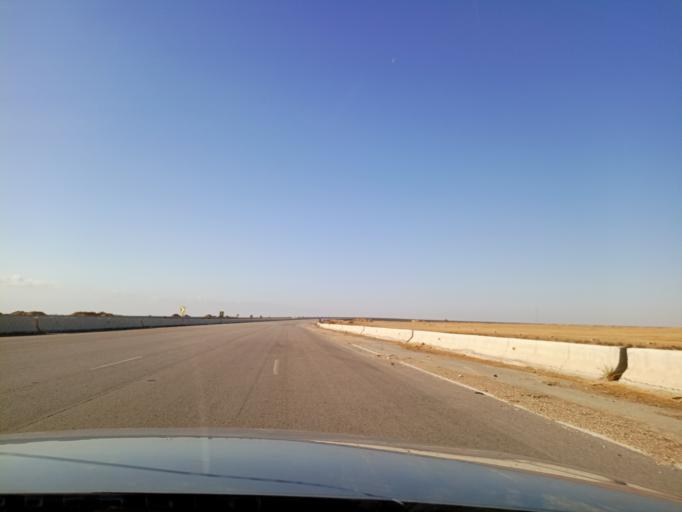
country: EG
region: Muhafazat al Fayyum
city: Tamiyah
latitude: 29.5708
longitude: 30.8378
